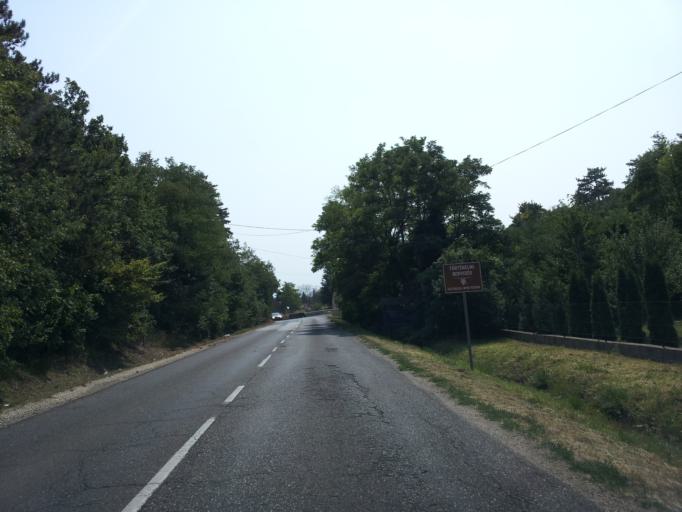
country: HU
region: Veszprem
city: Csopak
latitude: 46.9858
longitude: 17.9197
